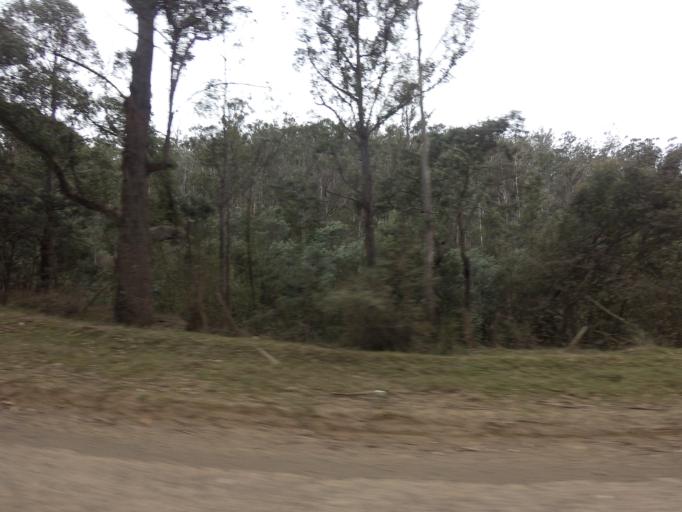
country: AU
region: Tasmania
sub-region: Derwent Valley
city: New Norfolk
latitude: -42.5903
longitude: 147.0264
